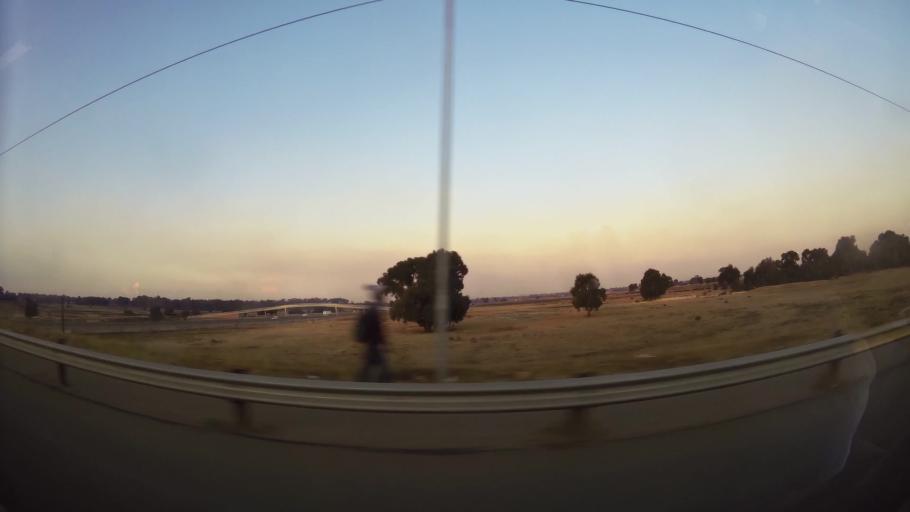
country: ZA
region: Gauteng
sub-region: Ekurhuleni Metropolitan Municipality
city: Springs
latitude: -26.2806
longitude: 28.4052
